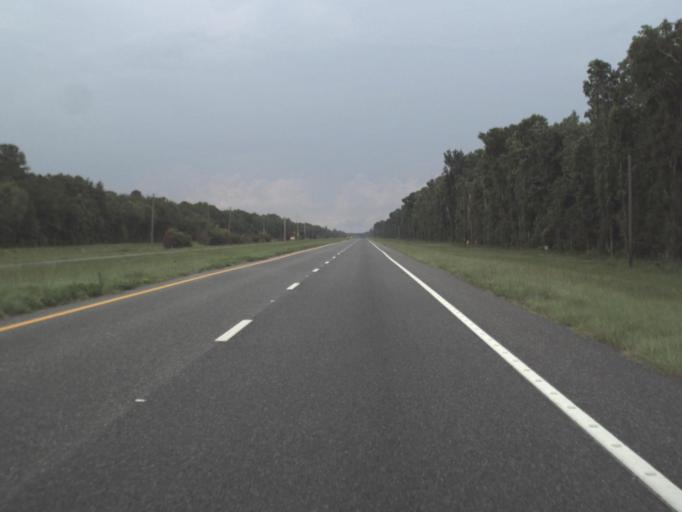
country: US
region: Florida
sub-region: Levy County
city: Inglis
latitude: 29.2272
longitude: -82.7075
